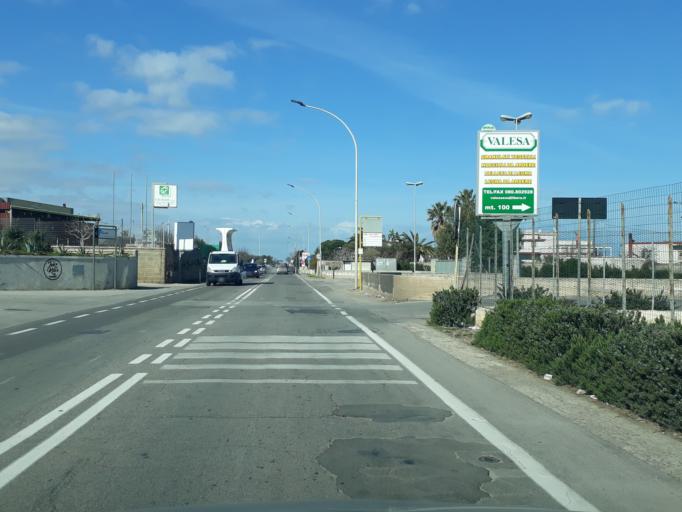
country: IT
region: Apulia
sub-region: Provincia di Bari
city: Monopoli
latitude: 40.9700
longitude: 17.2660
